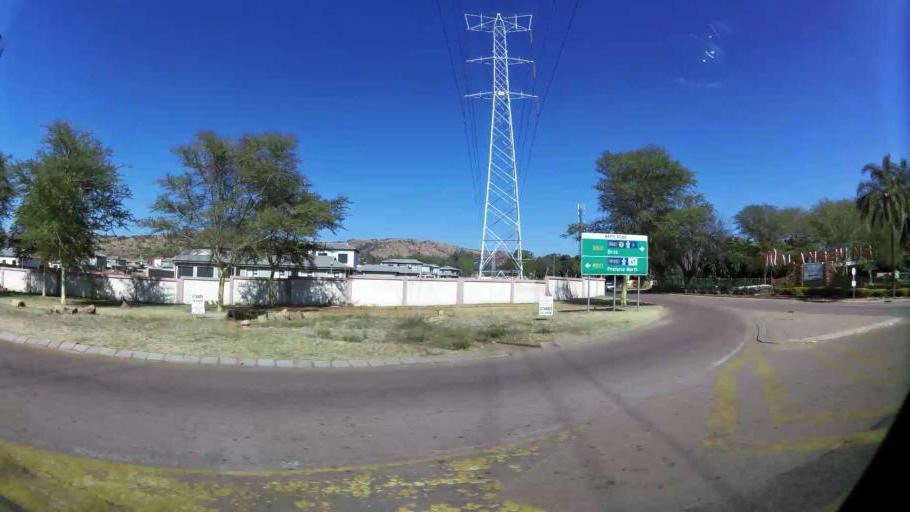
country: ZA
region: North-West
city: Ga-Rankuwa
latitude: -25.6671
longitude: 28.0782
